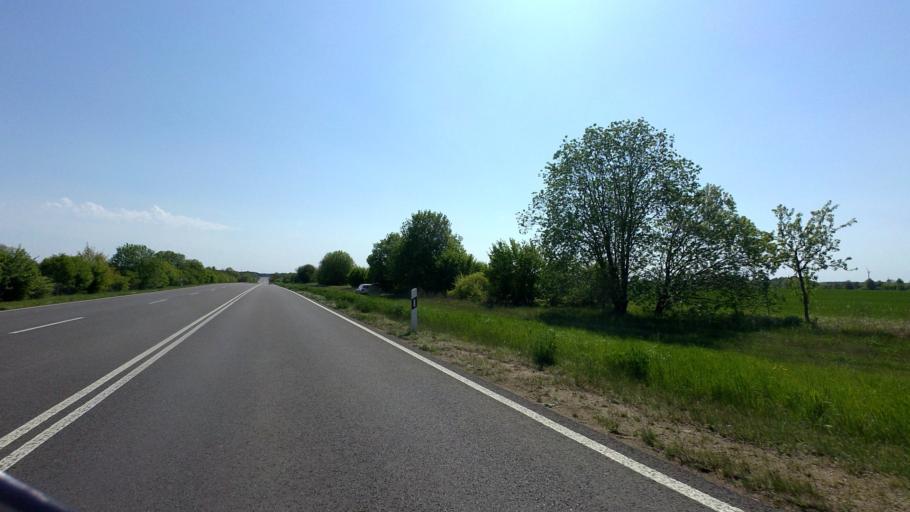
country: DE
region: Brandenburg
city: Beeskow
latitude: 52.1762
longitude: 14.2167
